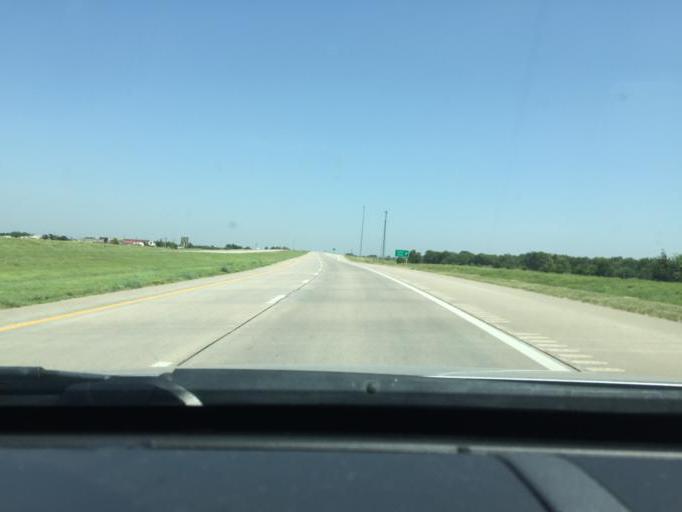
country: US
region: Kansas
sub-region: Reno County
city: Haven
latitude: 37.9366
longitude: -97.8744
